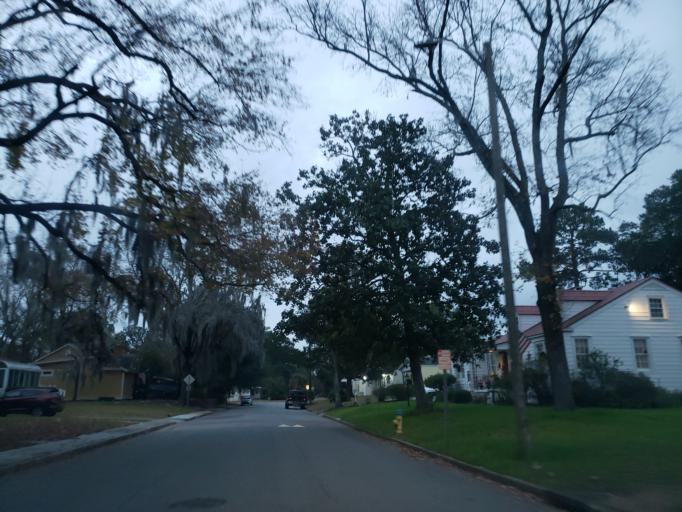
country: US
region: Georgia
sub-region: Chatham County
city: Thunderbolt
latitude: 32.0535
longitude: -81.0644
